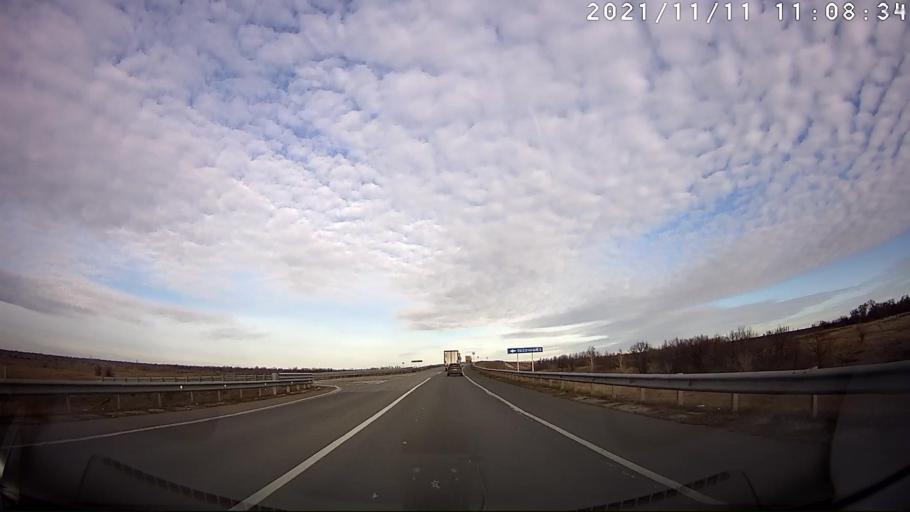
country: RU
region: Samara
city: Varlamovo
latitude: 53.1694
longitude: 48.2809
